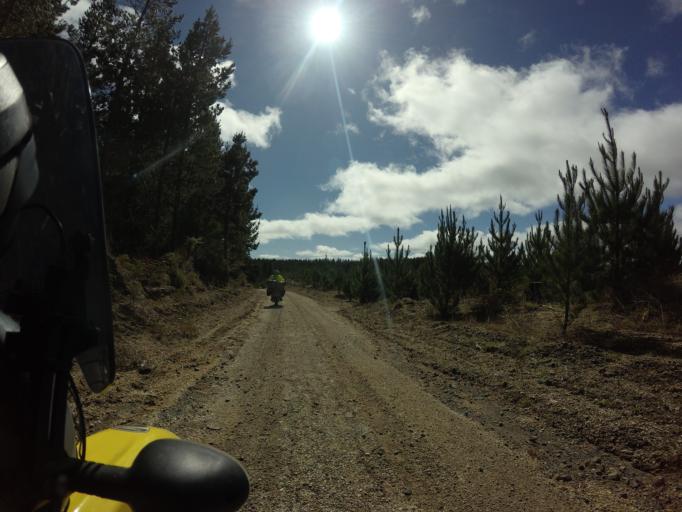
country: NZ
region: Bay of Plenty
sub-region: Whakatane District
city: Murupara
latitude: -38.8231
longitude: 176.5499
